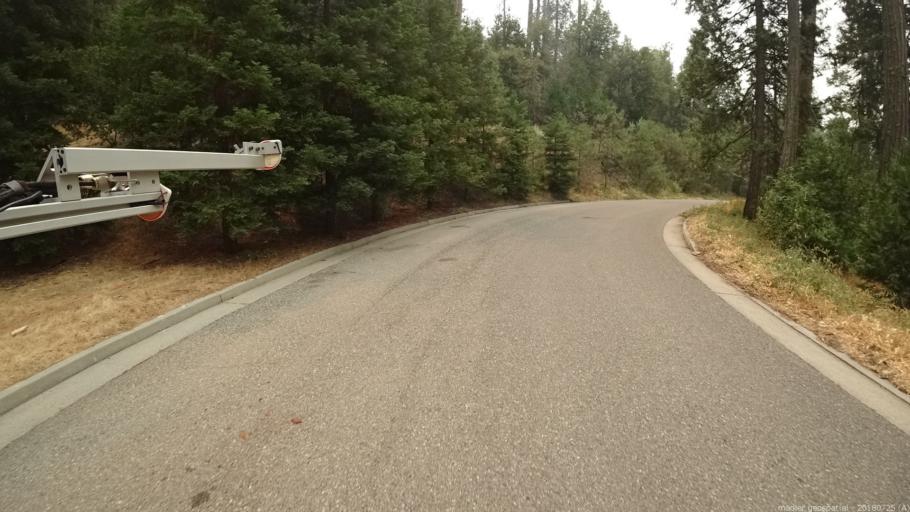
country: US
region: California
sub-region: Madera County
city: Oakhurst
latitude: 37.3266
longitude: -119.5645
